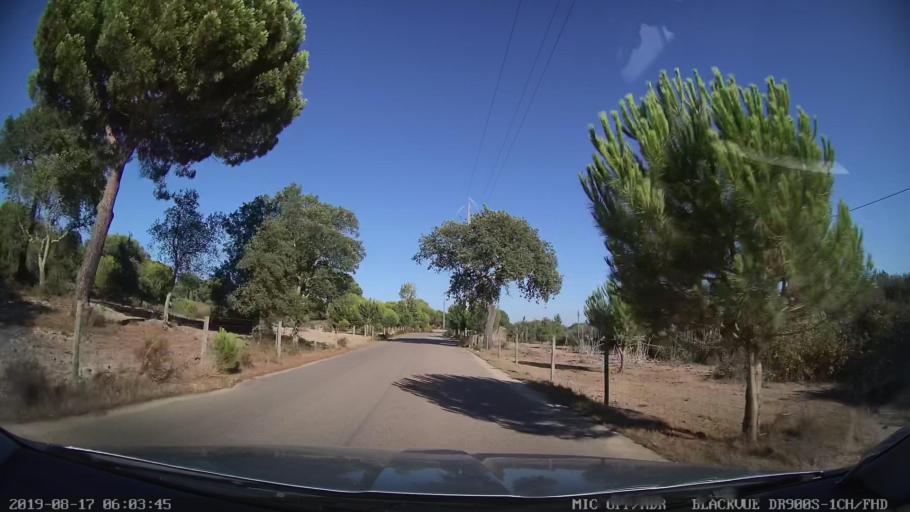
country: PT
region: Santarem
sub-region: Benavente
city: Poceirao
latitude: 38.8472
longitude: -8.7123
